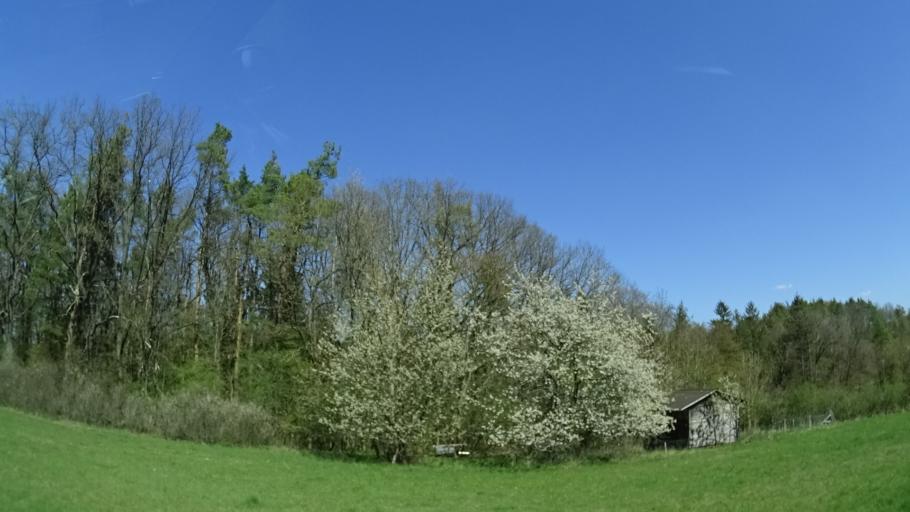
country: DE
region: Bavaria
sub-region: Upper Palatinate
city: Weigendorf
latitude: 49.4845
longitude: 11.5667
